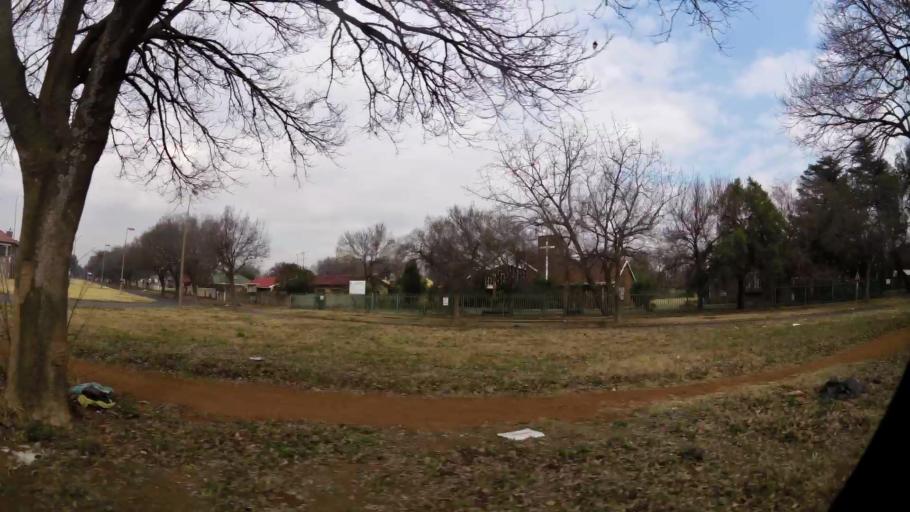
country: ZA
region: Gauteng
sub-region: Sedibeng District Municipality
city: Vanderbijlpark
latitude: -26.6929
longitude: 27.8309
